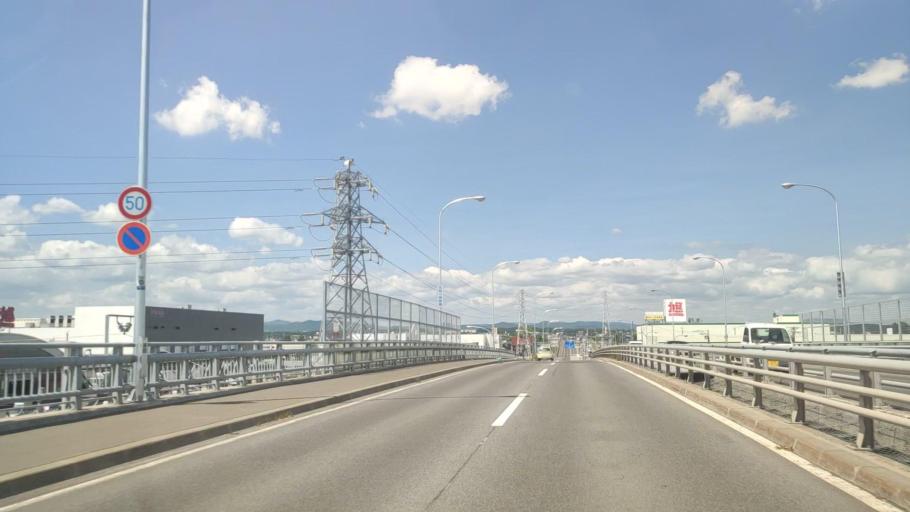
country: JP
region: Hokkaido
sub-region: Asahikawa-shi
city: Asahikawa
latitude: 43.7936
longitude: 142.4012
